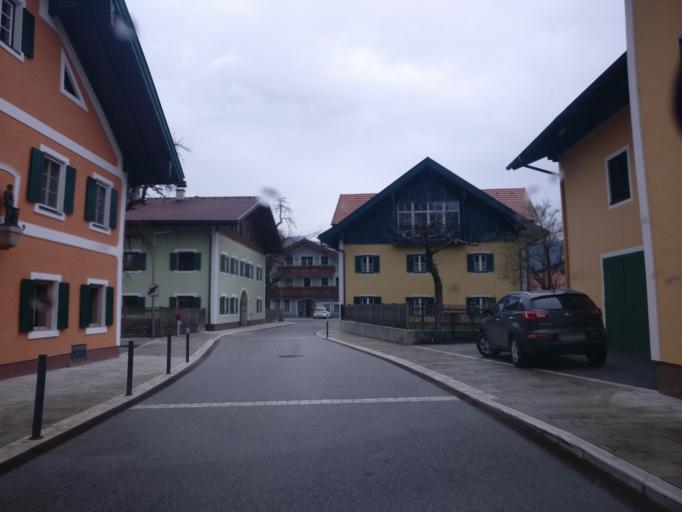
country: AT
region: Salzburg
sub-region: Politischer Bezirk Hallein
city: Kuchl
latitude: 47.6272
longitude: 13.1458
